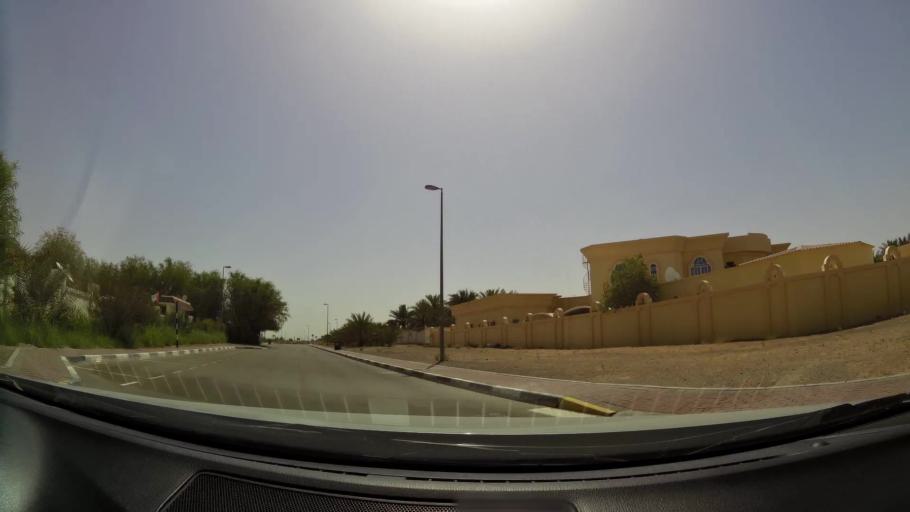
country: OM
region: Al Buraimi
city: Al Buraymi
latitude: 24.3000
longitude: 55.7568
